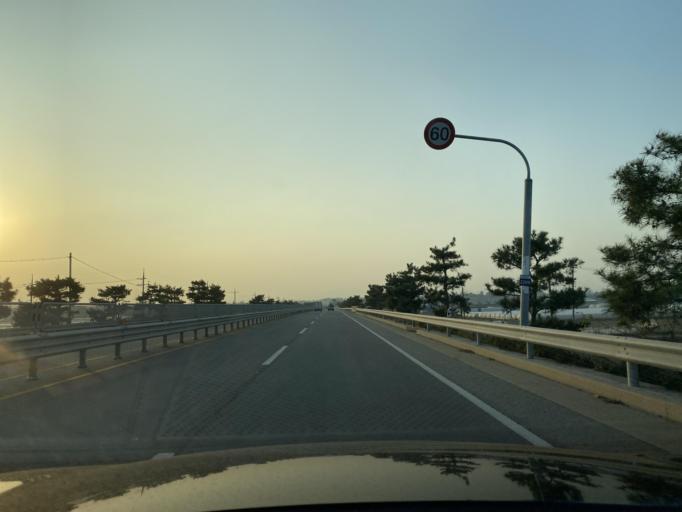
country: KR
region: Chungcheongnam-do
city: Yesan
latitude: 36.6968
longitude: 126.8094
